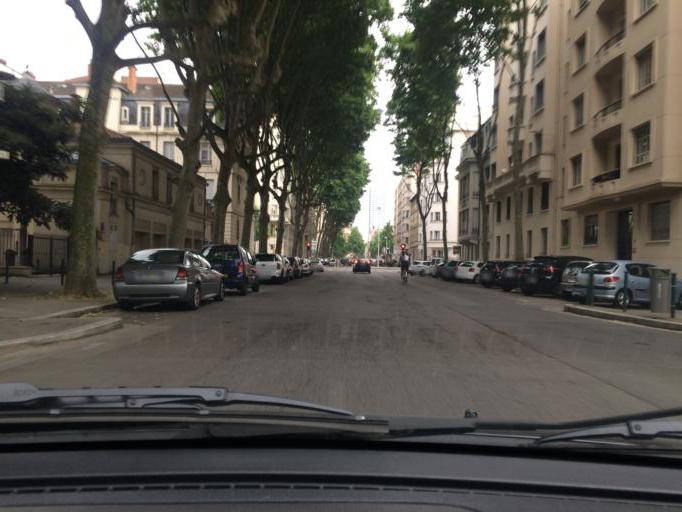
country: FR
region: Rhone-Alpes
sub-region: Departement du Rhone
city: Caluire-et-Cuire
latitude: 45.7740
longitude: 4.8496
